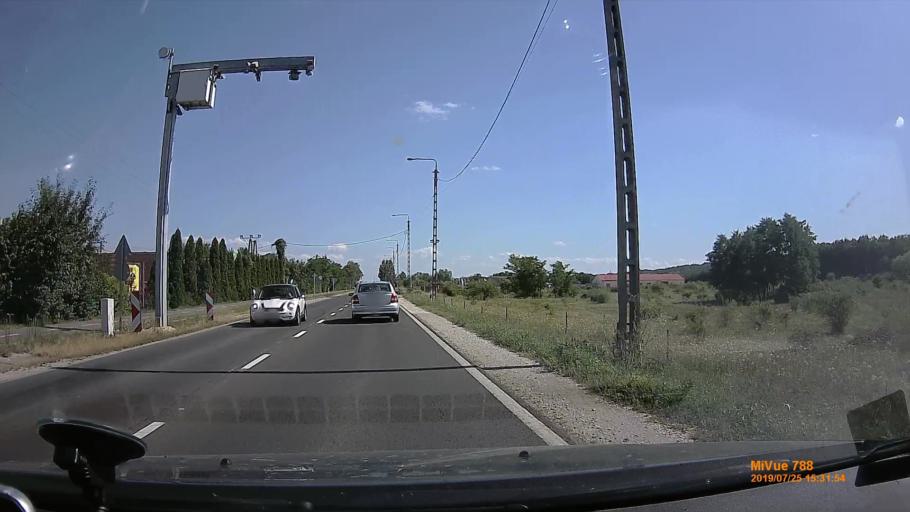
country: HU
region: Borsod-Abauj-Zemplen
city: Malyi
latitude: 48.0103
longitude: 20.8260
